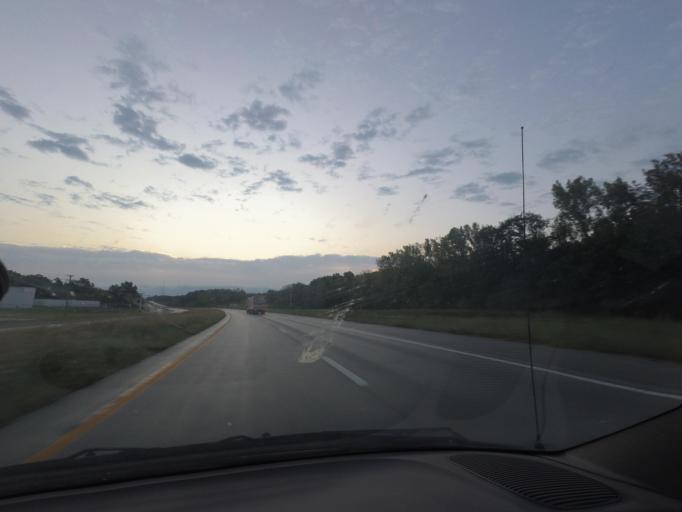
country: US
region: Missouri
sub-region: Macon County
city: Macon
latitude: 39.7461
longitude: -92.4941
